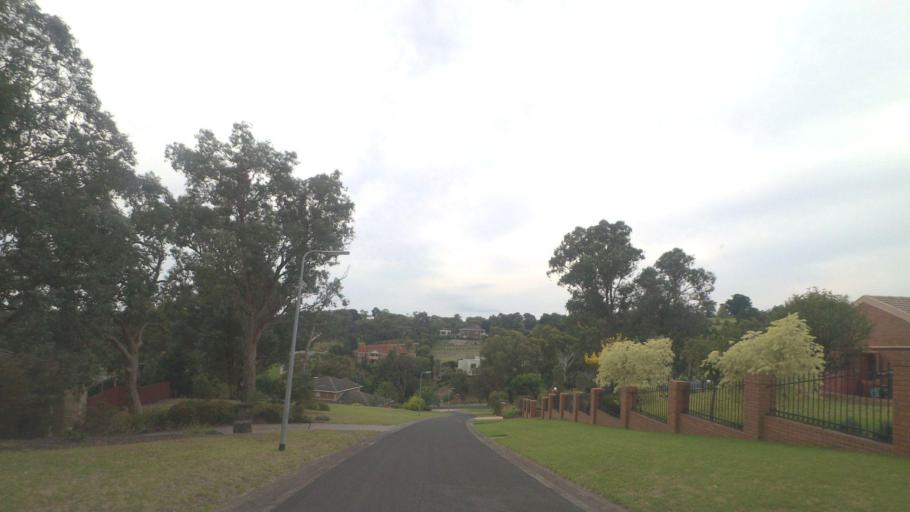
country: AU
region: Victoria
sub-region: Manningham
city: Park Orchards
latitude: -37.7526
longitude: 145.1896
